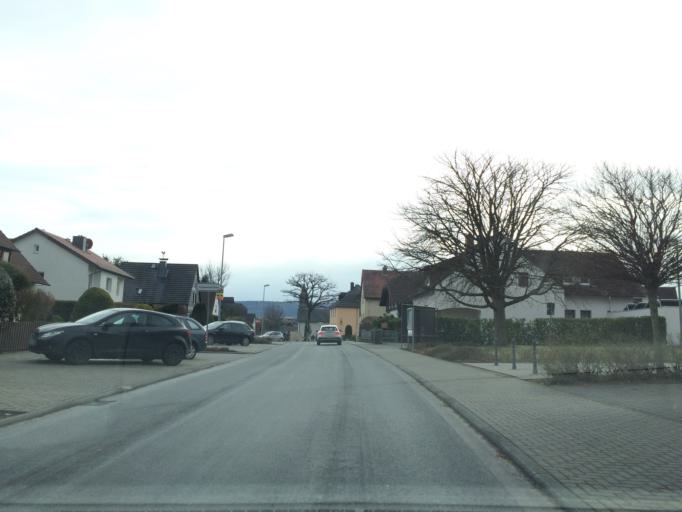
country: DE
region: Hesse
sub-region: Regierungsbezirk Darmstadt
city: Neu-Anspach
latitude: 50.3123
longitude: 8.5008
